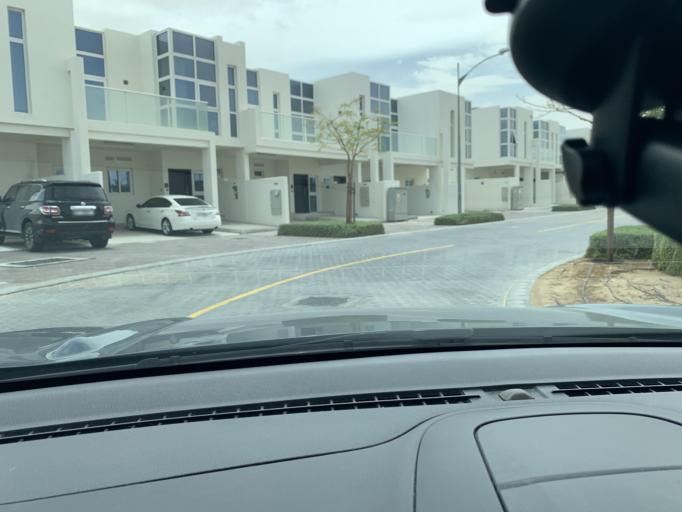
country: AE
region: Dubai
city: Dubai
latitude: 24.9943
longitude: 55.3733
